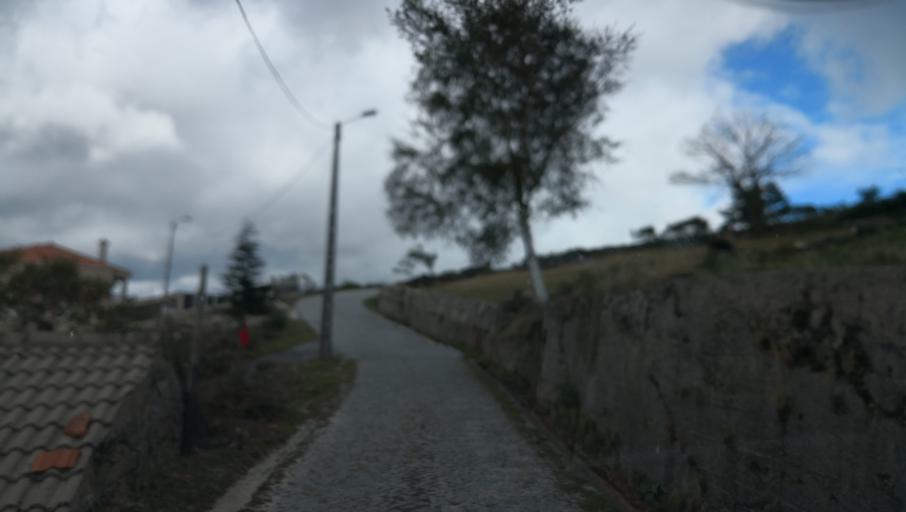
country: PT
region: Vila Real
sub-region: Vila Real
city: Vila Real
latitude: 41.3731
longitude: -7.8306
